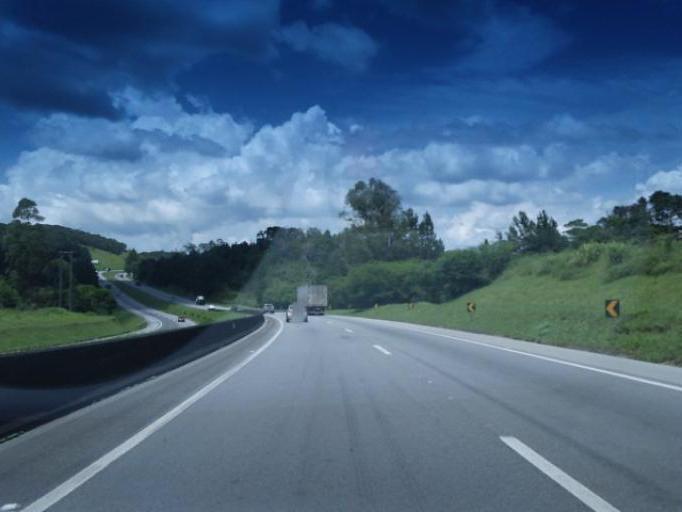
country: BR
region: Sao Paulo
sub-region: Juquitiba
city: Juquitiba
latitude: -23.9667
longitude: -47.1313
